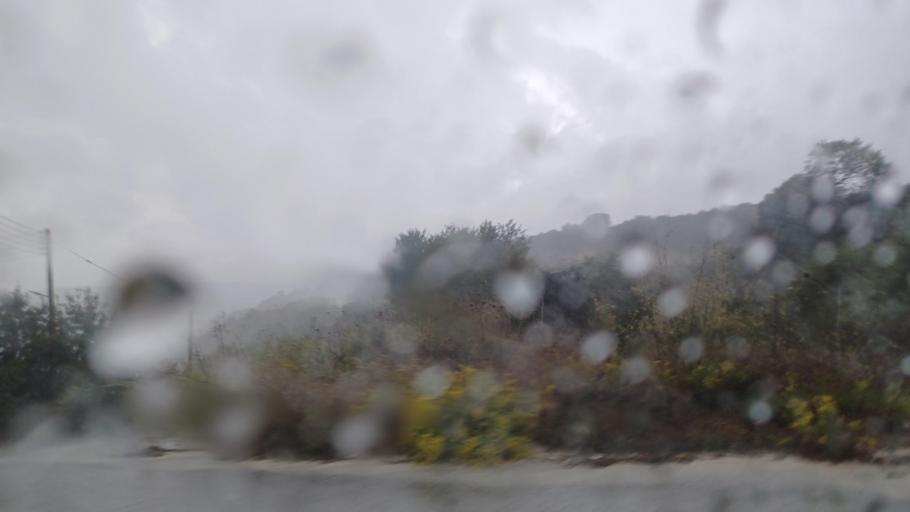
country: CY
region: Pafos
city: Tala
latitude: 34.8909
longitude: 32.4716
